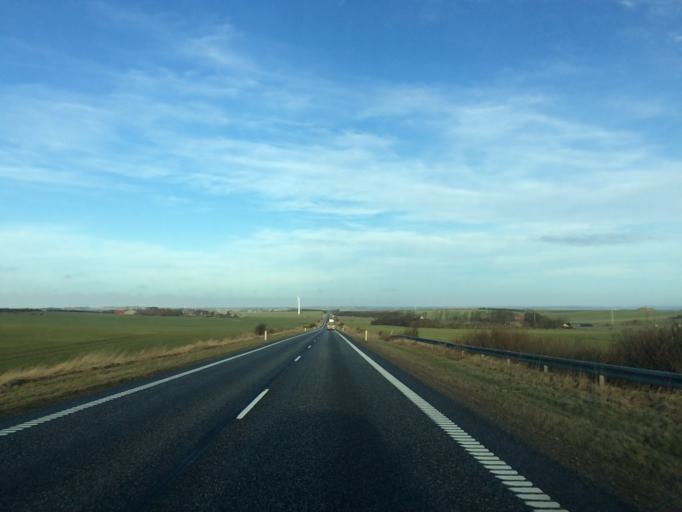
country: DK
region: North Denmark
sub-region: Thisted Kommune
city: Hurup
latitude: 56.7610
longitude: 8.4532
